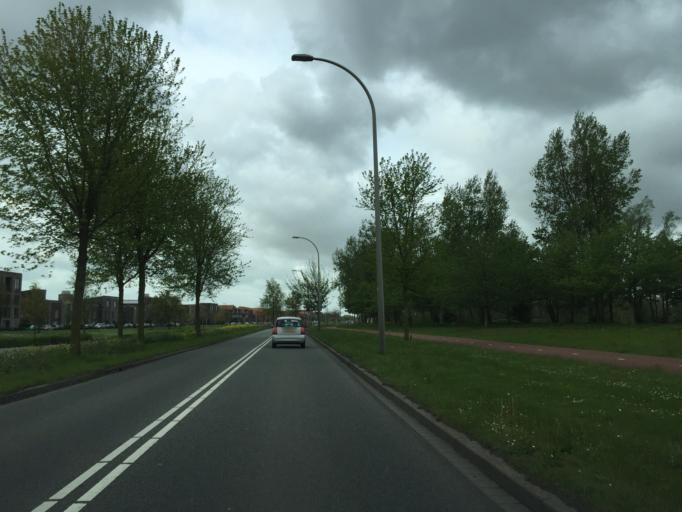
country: NL
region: South Holland
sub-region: Gemeente Den Haag
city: Ypenburg
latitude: 52.0488
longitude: 4.3742
